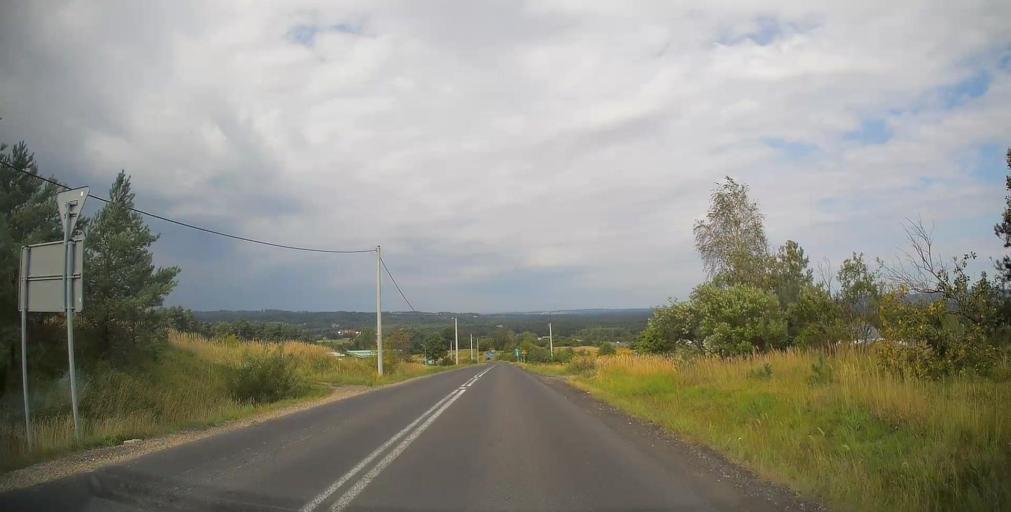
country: PL
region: Lesser Poland Voivodeship
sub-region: Powiat chrzanowski
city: Grojec
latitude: 50.0965
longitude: 19.5521
